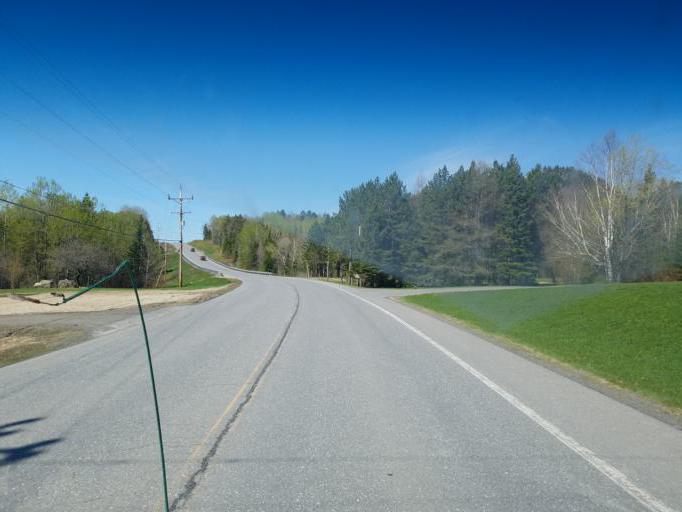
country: US
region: Maine
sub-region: Aroostook County
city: Presque Isle
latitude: 46.6665
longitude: -68.2228
